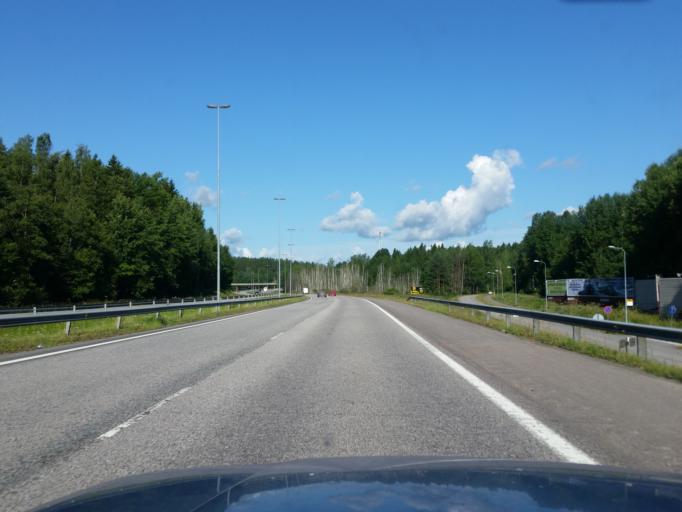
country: FI
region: Uusimaa
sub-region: Helsinki
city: Kirkkonummi
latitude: 60.2833
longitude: 24.4333
